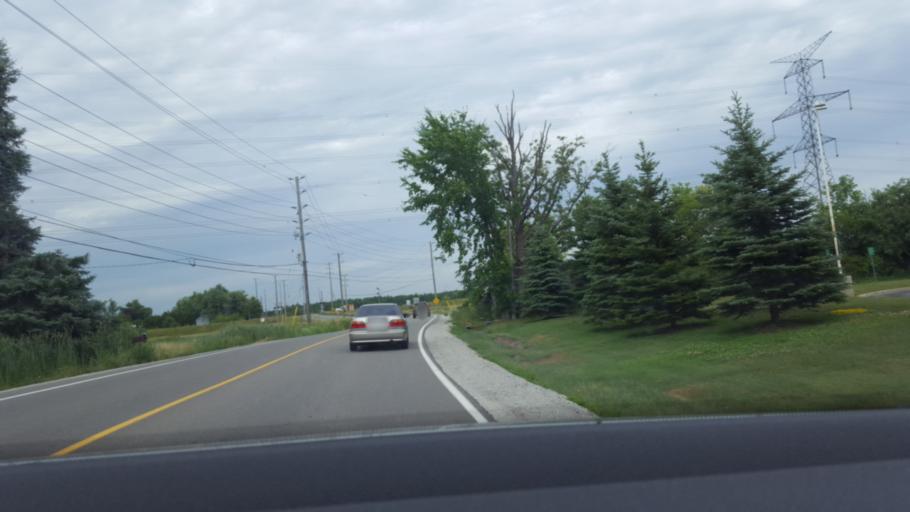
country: CA
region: Ontario
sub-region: Halton
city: Milton
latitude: 43.5448
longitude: -79.9168
